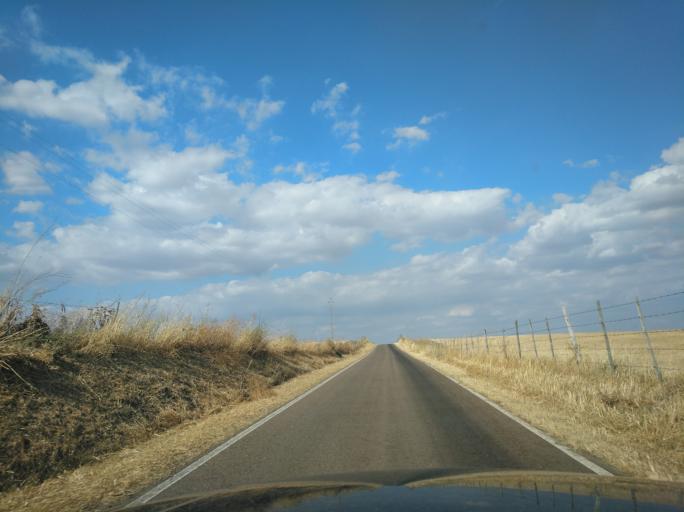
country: PT
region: Portalegre
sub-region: Campo Maior
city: Campo Maior
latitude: 38.9763
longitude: -7.0172
